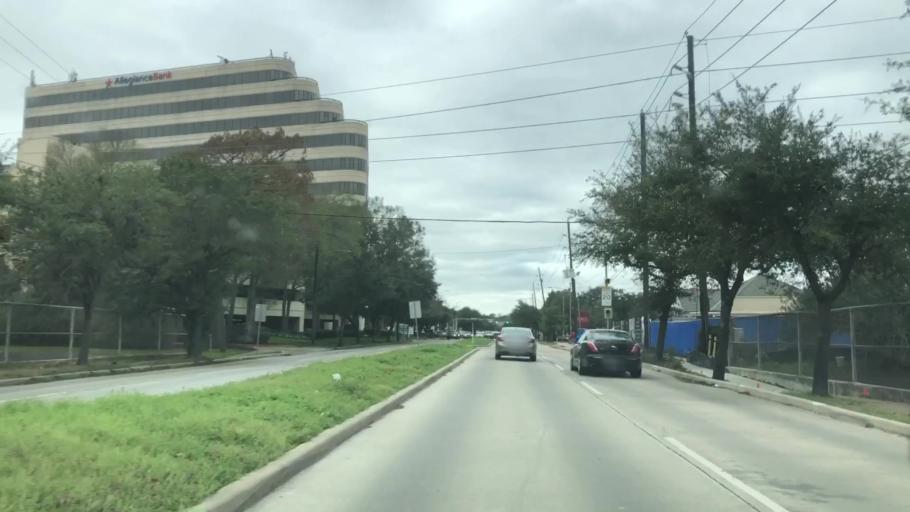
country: US
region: Texas
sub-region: Harris County
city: Hunters Creek Village
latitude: 29.7564
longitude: -95.4955
